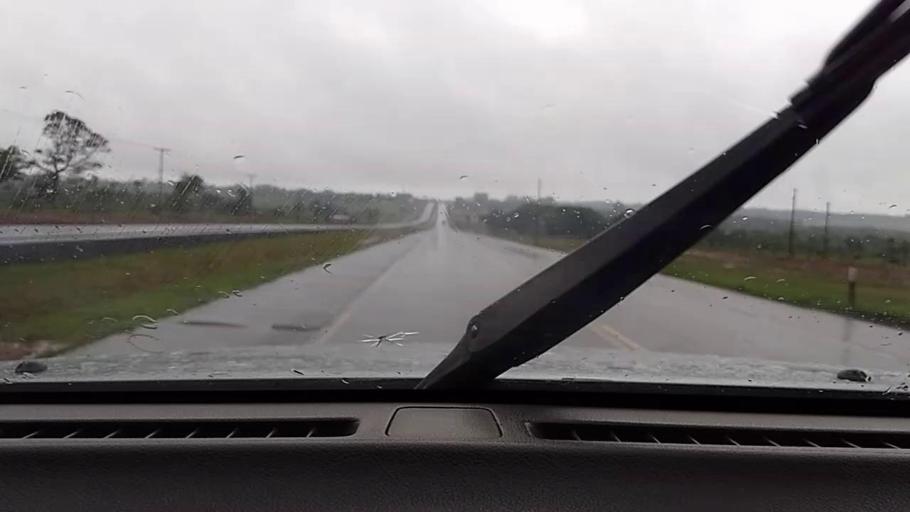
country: PY
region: Caaguazu
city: Repatriacion
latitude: -25.4658
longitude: -55.9507
